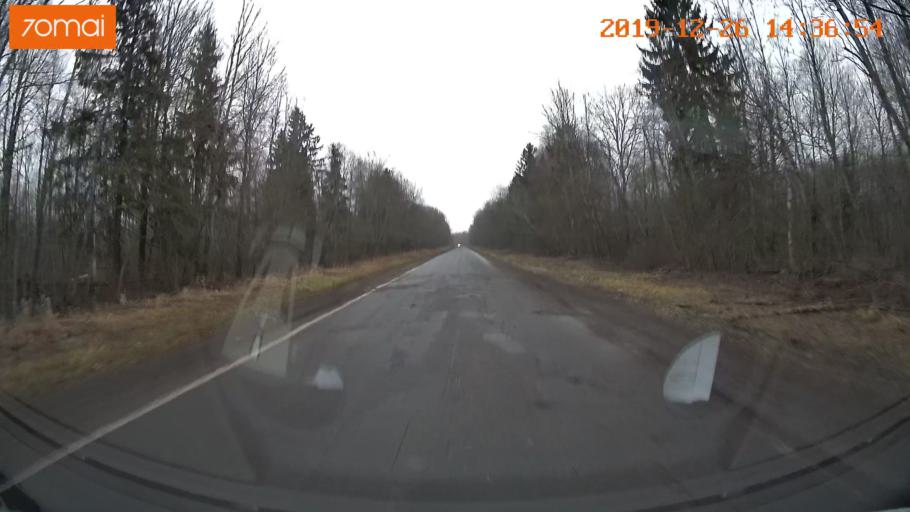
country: RU
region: Jaroslavl
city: Poshekhon'ye
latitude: 58.4073
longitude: 38.9744
